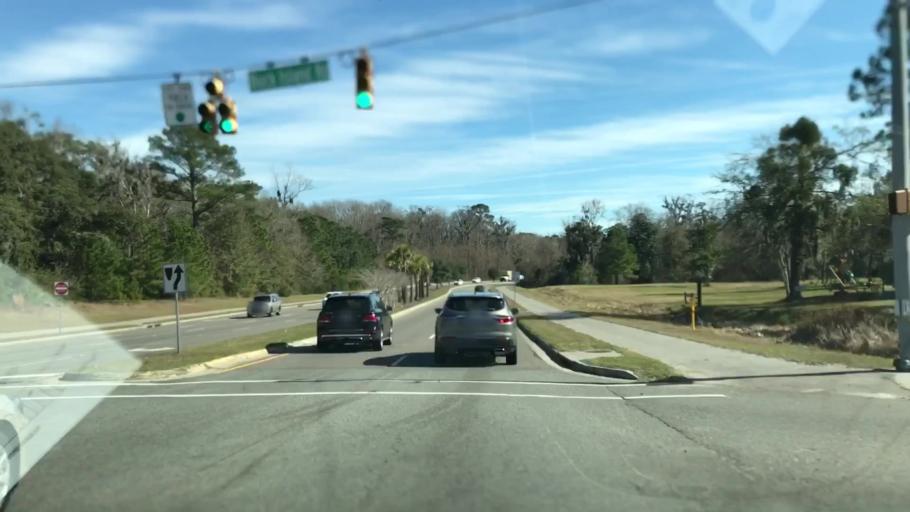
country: US
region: South Carolina
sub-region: Beaufort County
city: Bluffton
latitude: 32.2649
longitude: -80.8816
